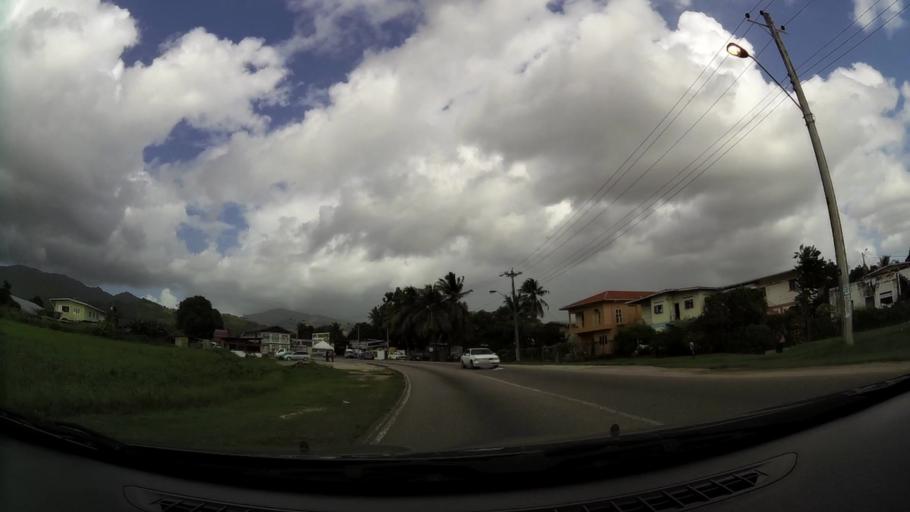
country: TT
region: Tunapuna/Piarco
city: Arouca
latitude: 10.6351
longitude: -61.3452
